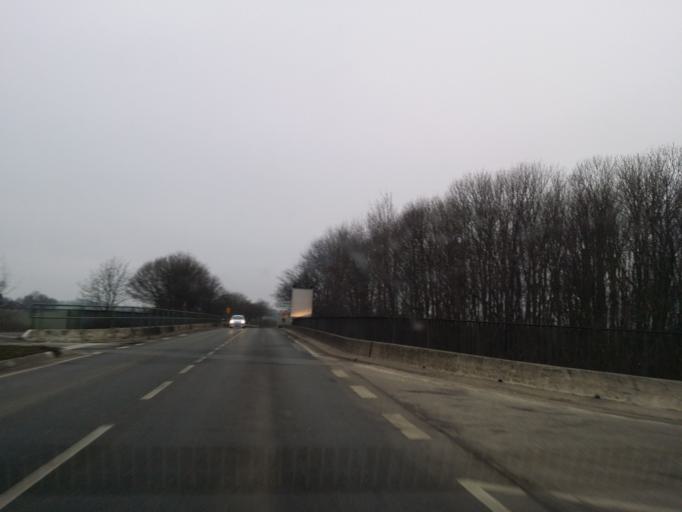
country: DE
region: Schleswig-Holstein
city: Fehmarn
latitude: 54.4455
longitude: 11.1701
